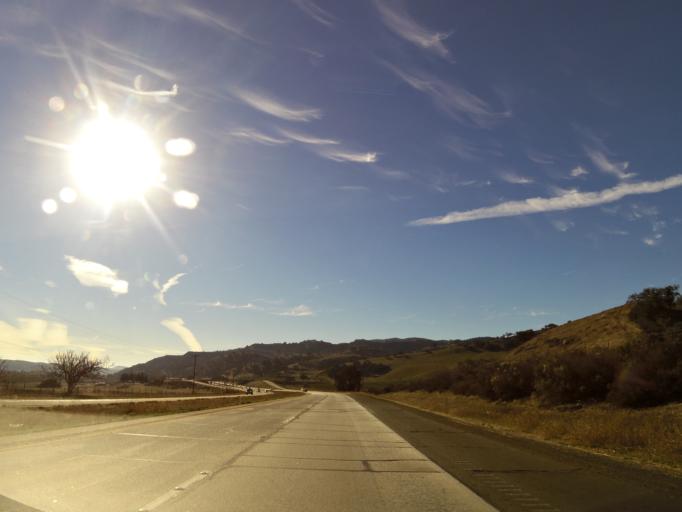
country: US
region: California
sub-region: San Luis Obispo County
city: Lake Nacimiento
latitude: 35.9814
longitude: -120.9024
